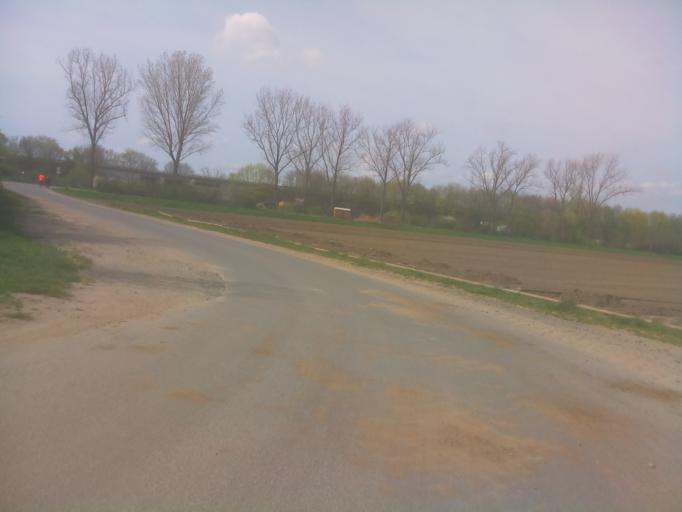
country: DE
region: Hesse
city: Lampertheim
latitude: 49.6084
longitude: 8.4670
